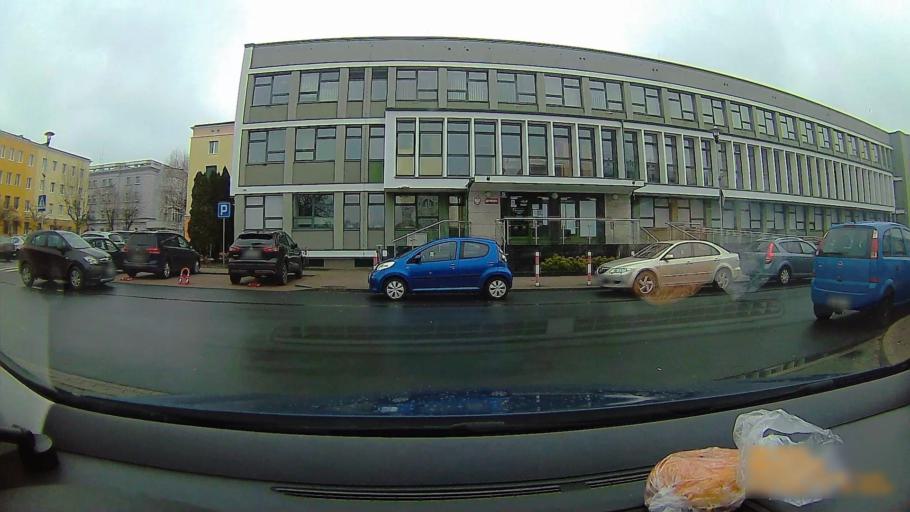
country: PL
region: Greater Poland Voivodeship
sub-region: Konin
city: Konin
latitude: 52.2274
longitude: 18.2523
